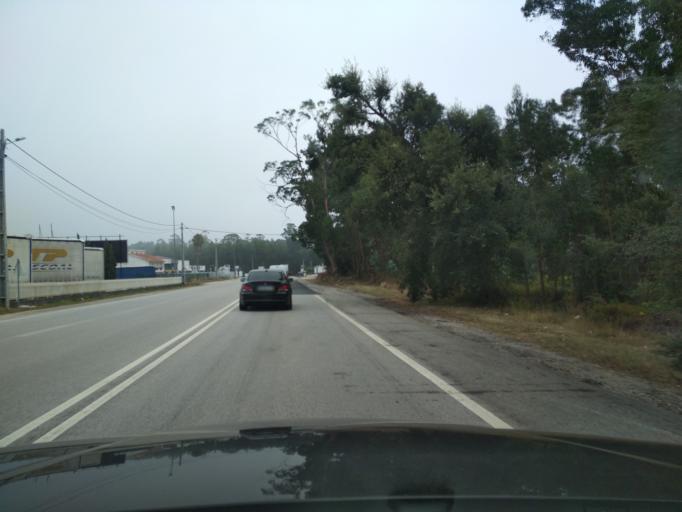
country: PT
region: Aveiro
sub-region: Mealhada
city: Pampilhosa do Botao
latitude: 40.3397
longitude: -8.4520
